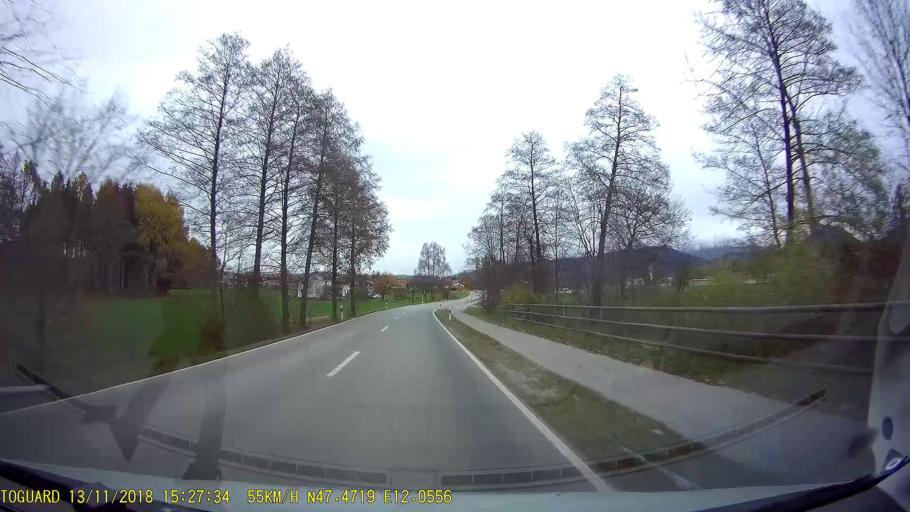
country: DE
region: Bavaria
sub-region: Upper Bavaria
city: Raubling
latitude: 47.7866
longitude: 12.0954
